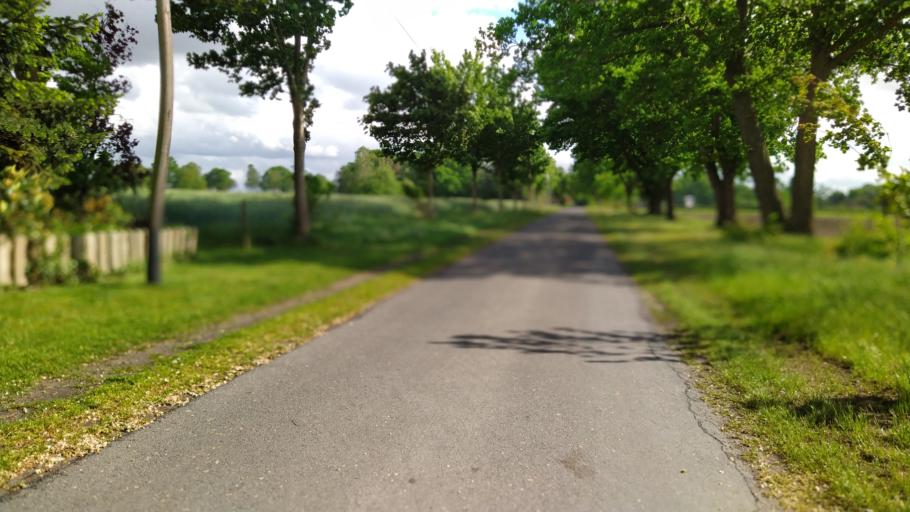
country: DE
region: Lower Saxony
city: Brest
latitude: 53.4552
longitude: 9.3917
